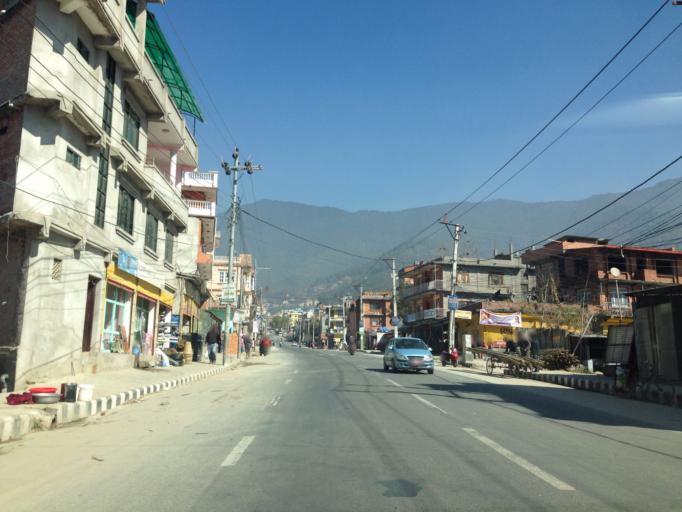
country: NP
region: Central Region
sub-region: Bagmati Zone
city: Kathmandu
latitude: 27.7722
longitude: 85.3594
